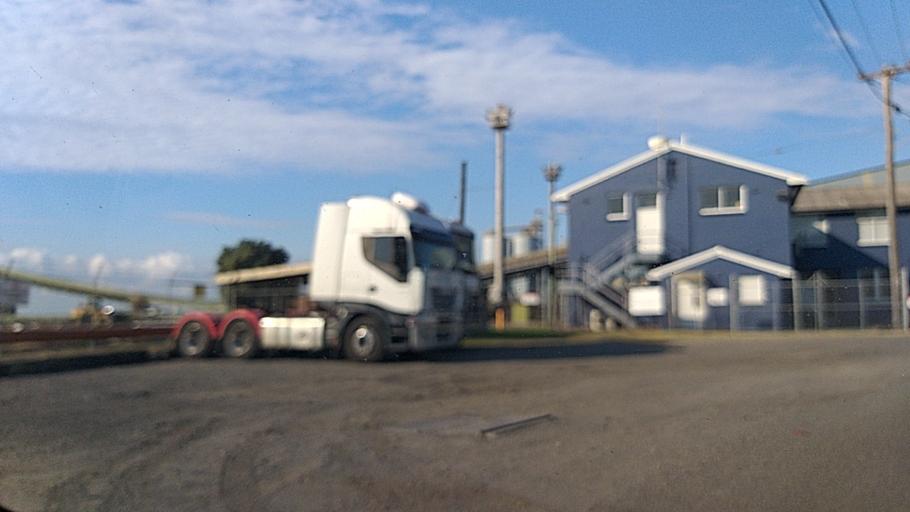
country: AU
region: New South Wales
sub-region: Wollongong
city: Port Kembla
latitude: -34.4682
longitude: 150.9003
